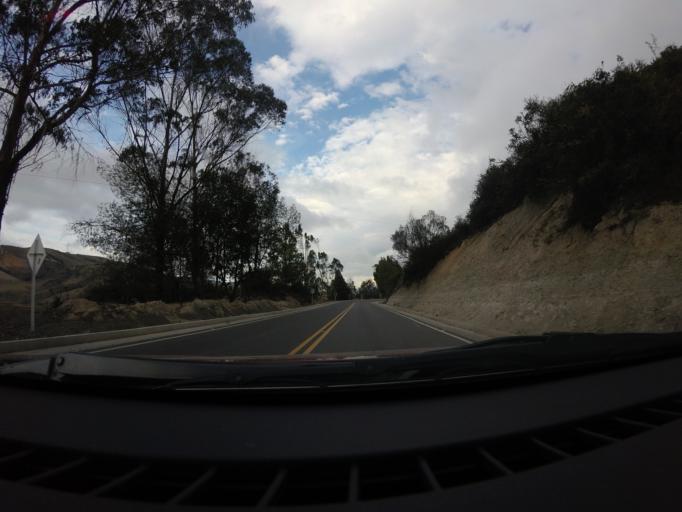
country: CO
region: Boyaca
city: Cucaita
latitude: 5.5596
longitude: -73.4091
